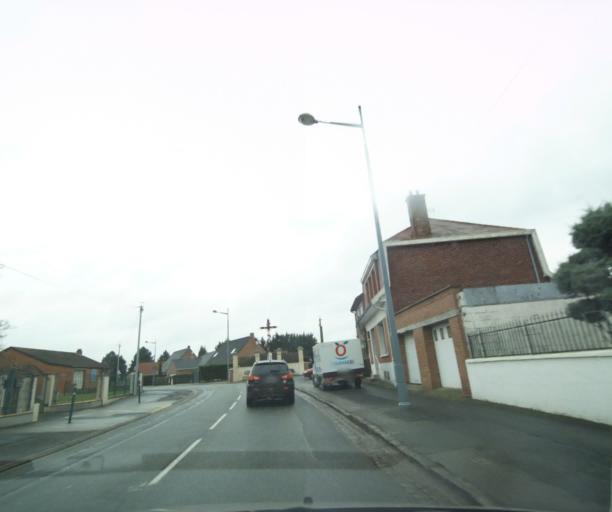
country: FR
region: Nord-Pas-de-Calais
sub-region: Departement du Nord
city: Prouvy
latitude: 50.3226
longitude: 3.4522
